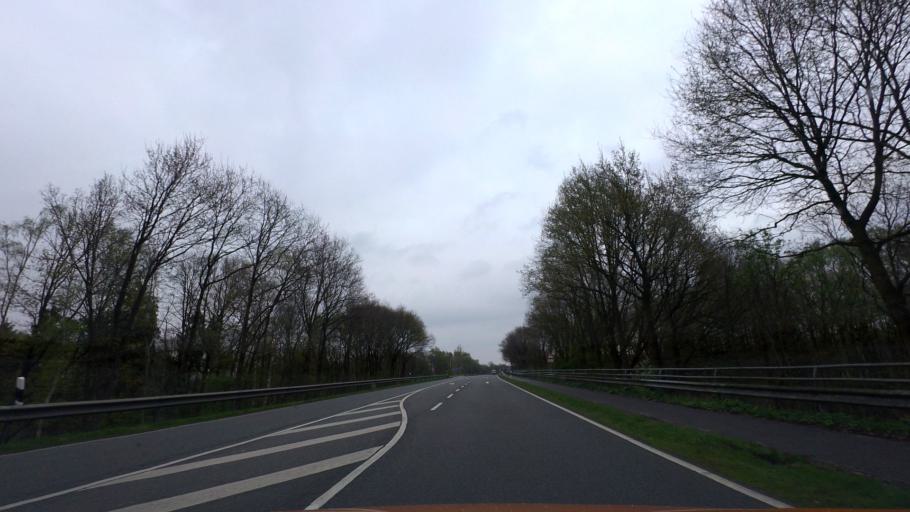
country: DE
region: Lower Saxony
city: Holdorf
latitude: 52.5970
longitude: 8.1097
